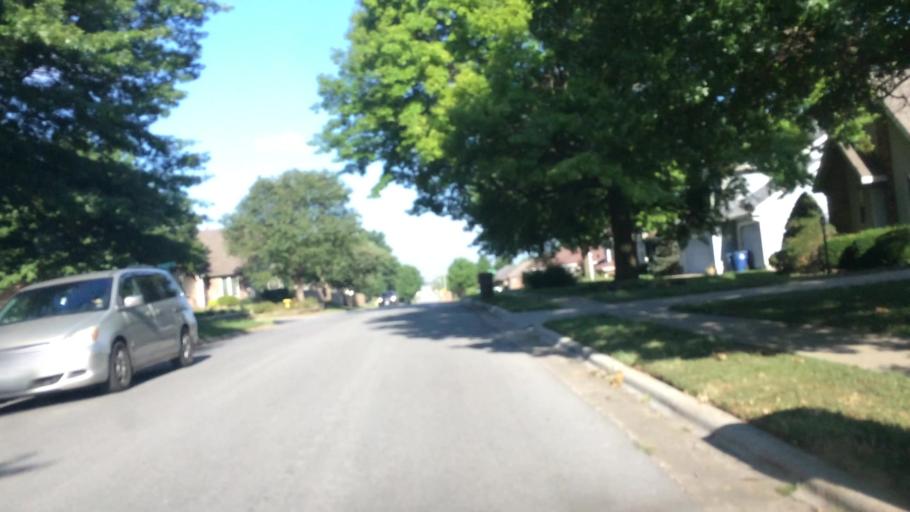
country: US
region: Missouri
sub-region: Greene County
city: Springfield
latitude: 37.2661
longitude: -93.2675
